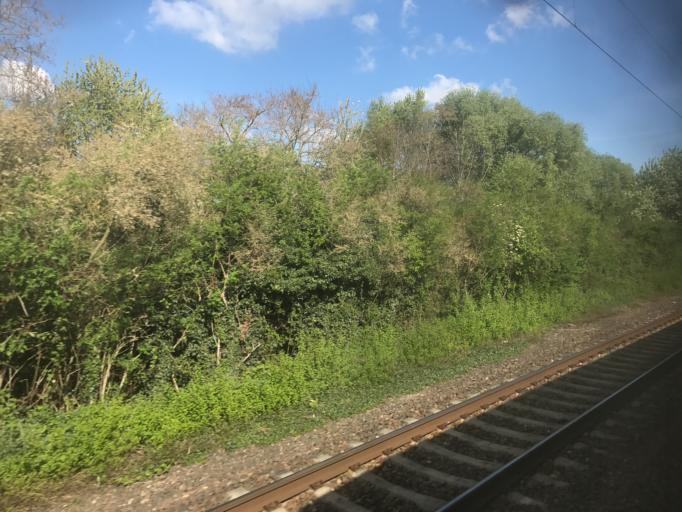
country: DE
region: Rheinland-Pfalz
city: Guntersblum
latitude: 49.7884
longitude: 8.3500
